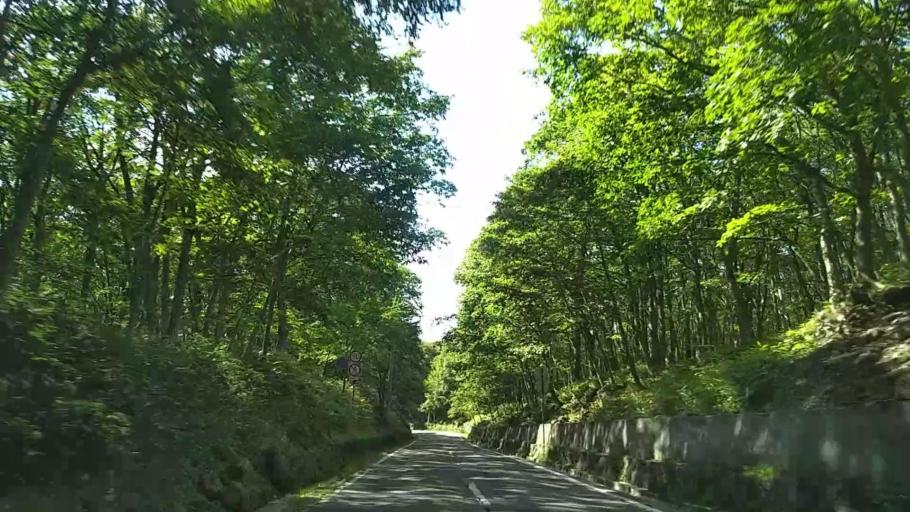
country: JP
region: Nagano
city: Chino
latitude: 36.0957
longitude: 138.2750
